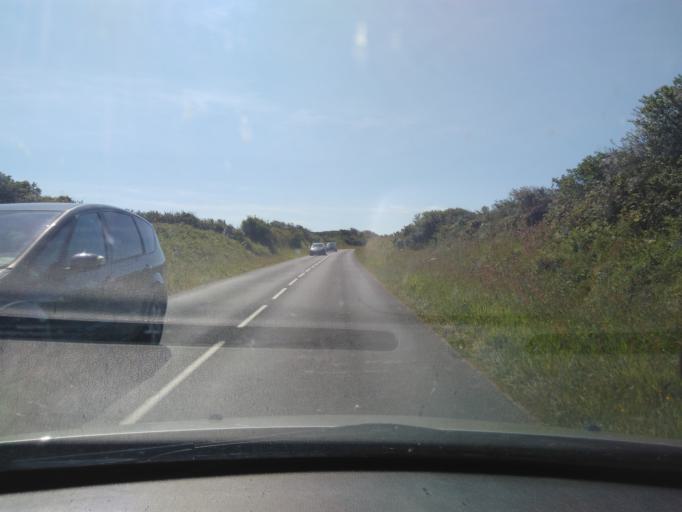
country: FR
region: Lower Normandy
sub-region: Departement de la Manche
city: Beaumont-Hague
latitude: 49.7007
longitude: -1.9275
